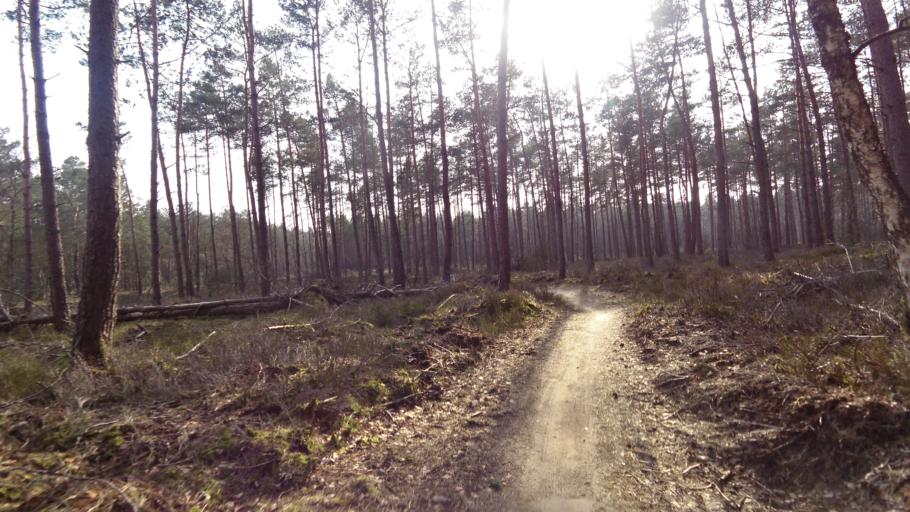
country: NL
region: Gelderland
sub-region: Gemeente Ede
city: Otterlo
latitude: 52.0861
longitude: 5.7417
